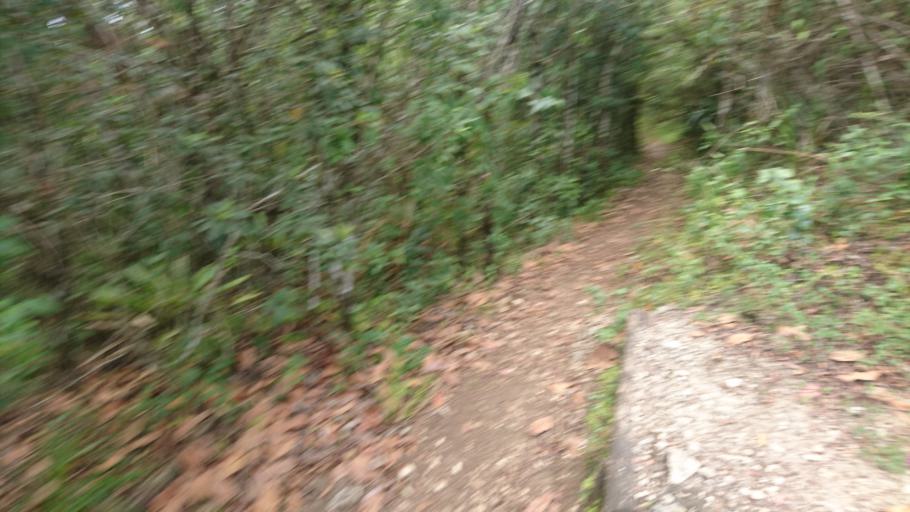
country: GT
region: Huehuetenango
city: Union
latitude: 16.1116
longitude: -91.6730
